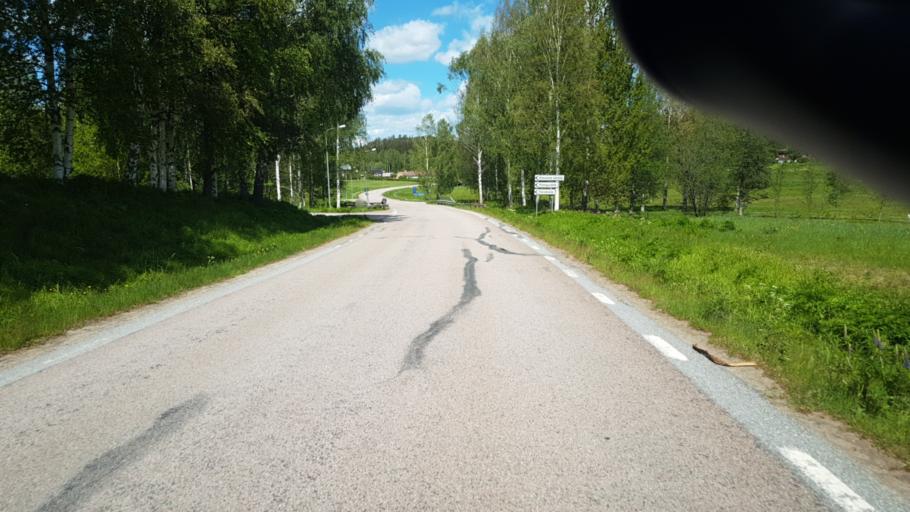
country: SE
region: Vaermland
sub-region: Arvika Kommun
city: Arvika
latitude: 59.7412
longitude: 12.8116
